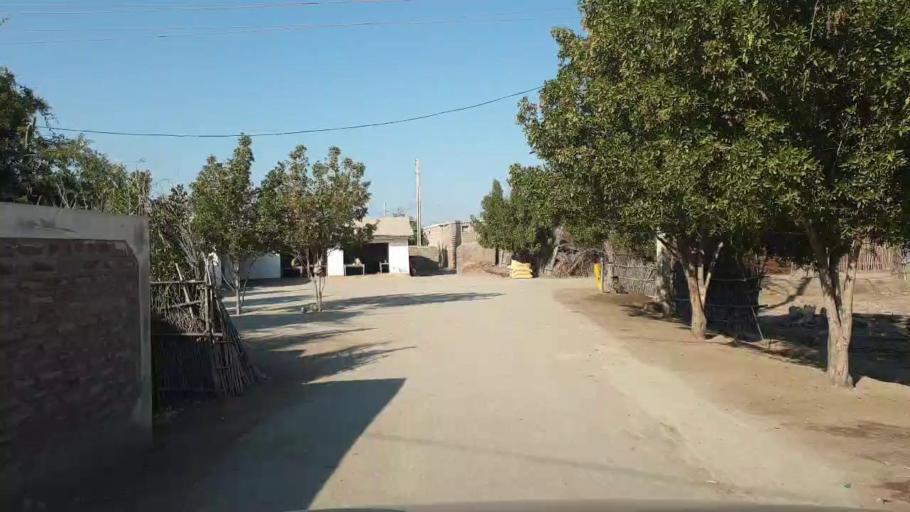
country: PK
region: Sindh
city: Khadro
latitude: 26.1544
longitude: 68.6853
